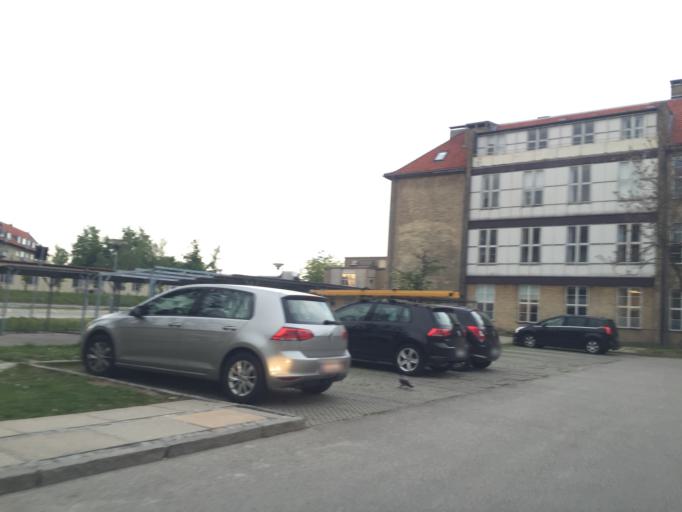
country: DK
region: Capital Region
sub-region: Gentofte Kommune
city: Charlottenlund
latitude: 55.7389
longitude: 12.5448
